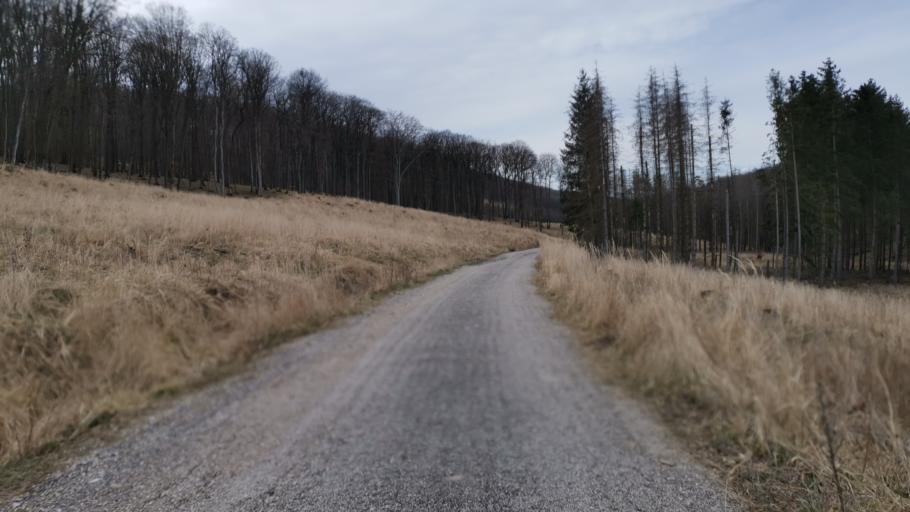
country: CZ
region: South Moravian
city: Straznice
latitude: 48.8289
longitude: 17.3362
